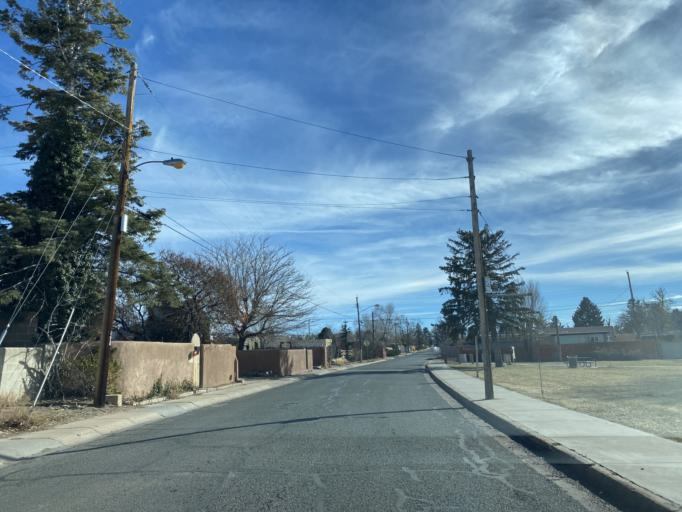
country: US
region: New Mexico
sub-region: Santa Fe County
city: Santa Fe
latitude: 35.6676
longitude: -105.9754
